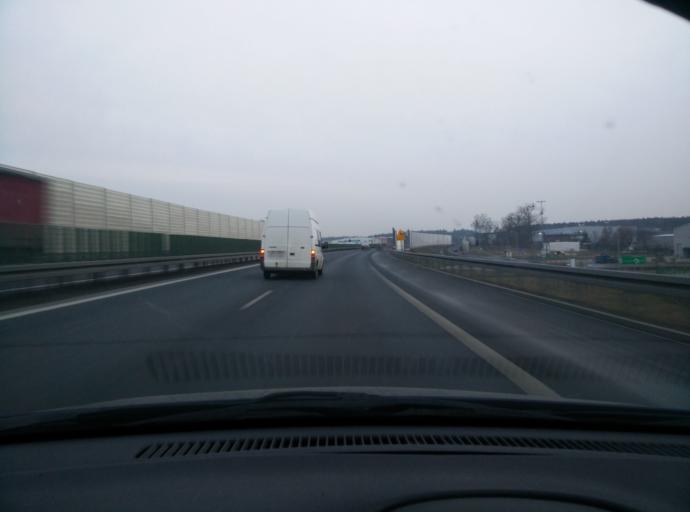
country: PL
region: Greater Poland Voivodeship
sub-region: Powiat poznanski
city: Kornik
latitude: 52.3127
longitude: 17.0452
